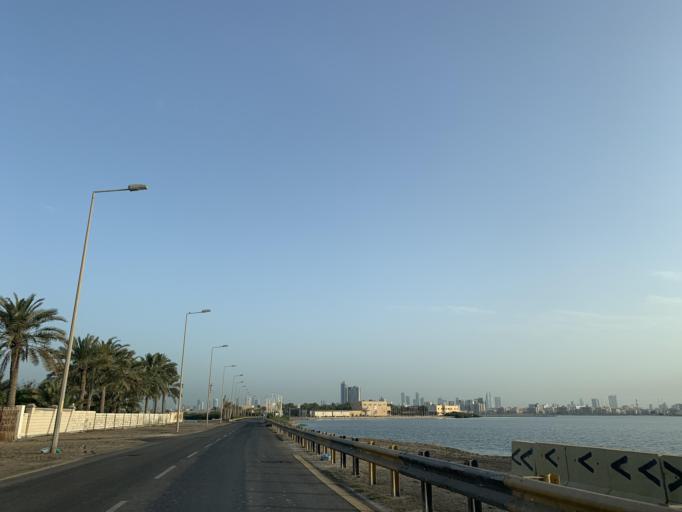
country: BH
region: Manama
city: Manama
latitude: 26.1860
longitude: 50.5868
